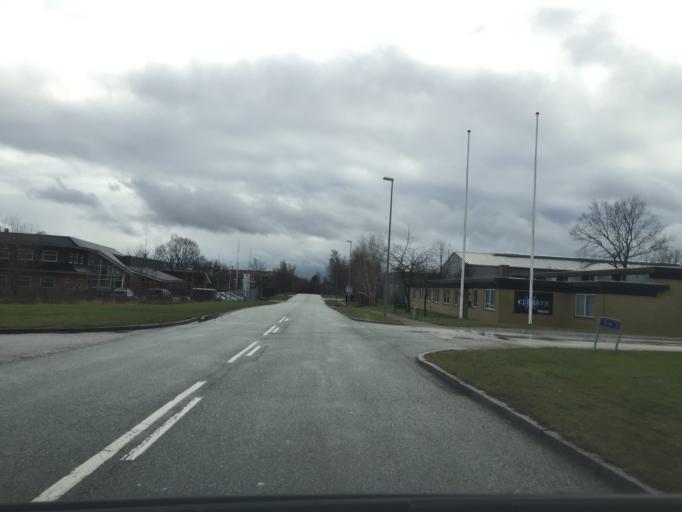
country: DK
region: Capital Region
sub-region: Fureso Kommune
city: Farum
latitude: 55.8213
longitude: 12.3628
